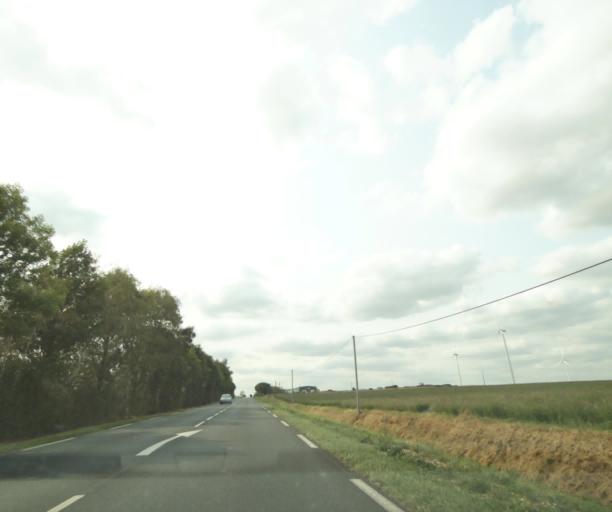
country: FR
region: Centre
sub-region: Departement de l'Indre
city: Buzancais
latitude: 46.9035
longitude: 1.3595
